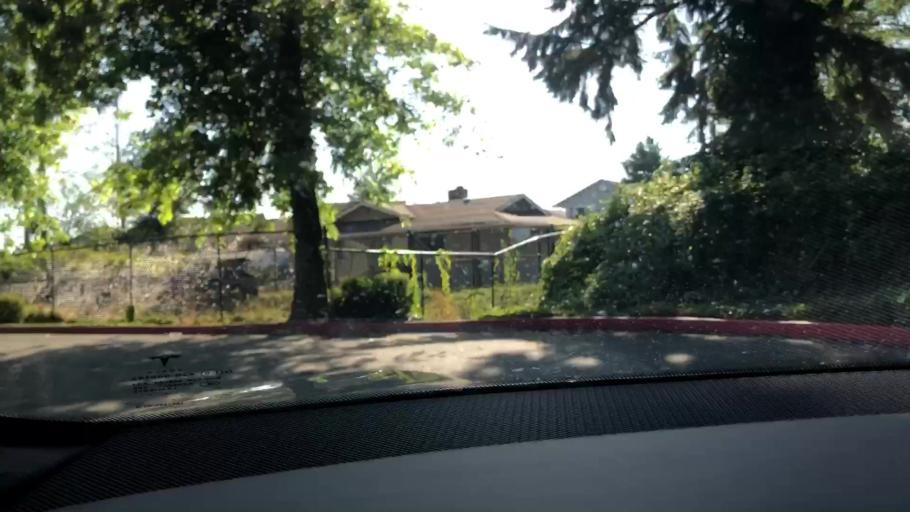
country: US
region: Washington
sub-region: Snohomish County
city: Mill Creek
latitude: 47.9120
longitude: -122.2206
